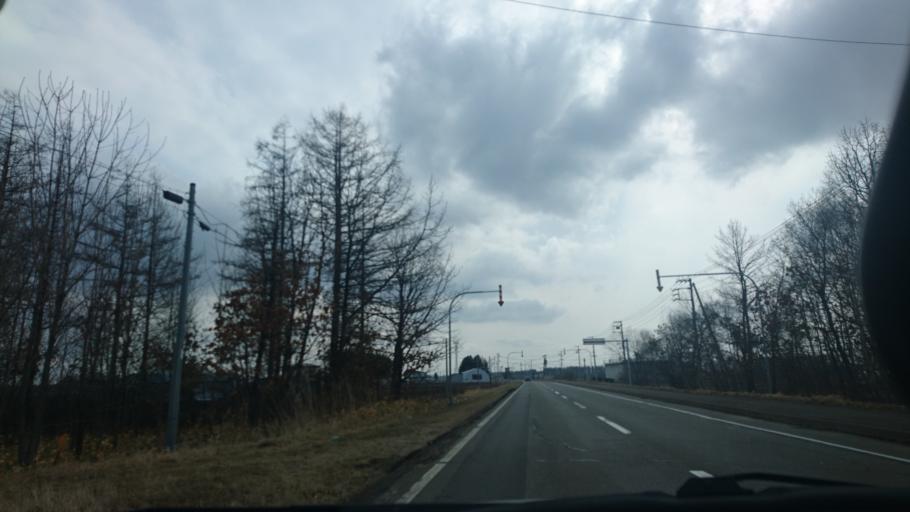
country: JP
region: Hokkaido
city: Otofuke
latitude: 43.2101
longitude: 143.2771
